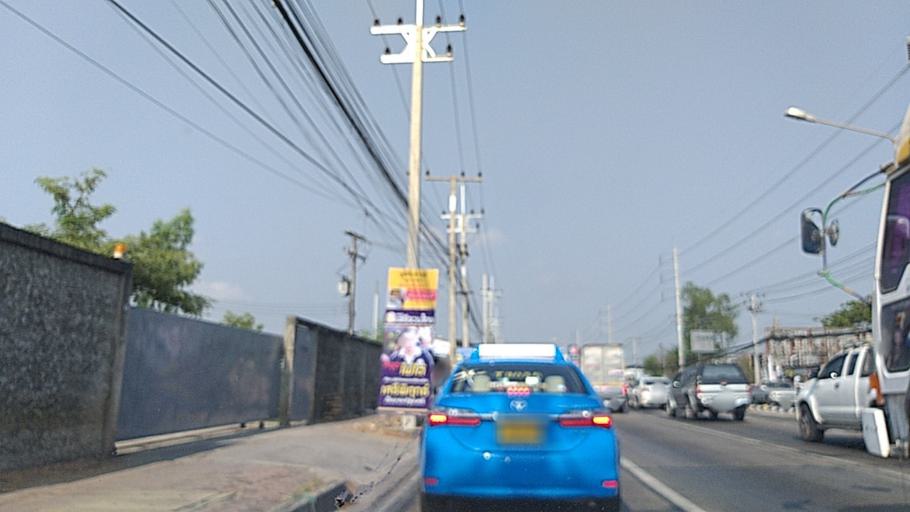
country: TH
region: Bangkok
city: Sai Mai
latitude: 13.9331
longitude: 100.6943
